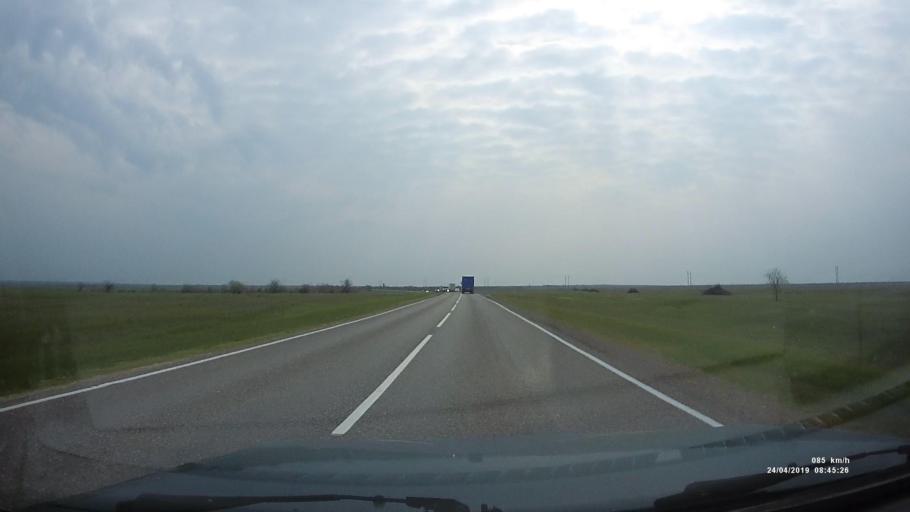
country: RU
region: Kalmykiya
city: Arshan'
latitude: 46.2361
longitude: 44.0606
